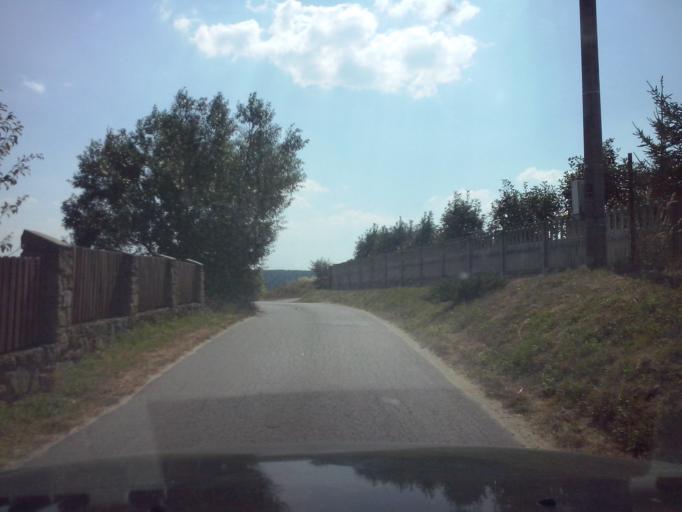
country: PL
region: Swietokrzyskie
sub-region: Powiat kielecki
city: Rakow
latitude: 50.6709
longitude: 21.0425
